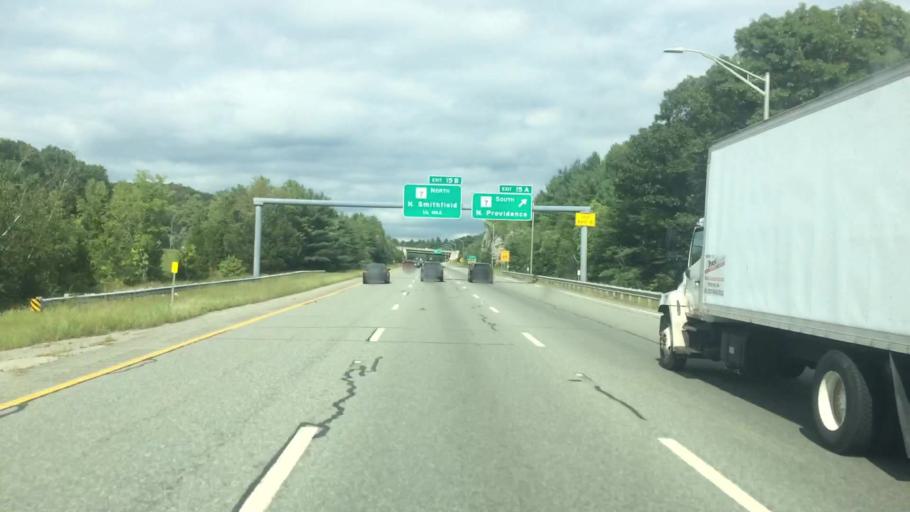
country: US
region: Rhode Island
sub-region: Providence County
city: Smithfield
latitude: 41.9042
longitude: -71.5166
